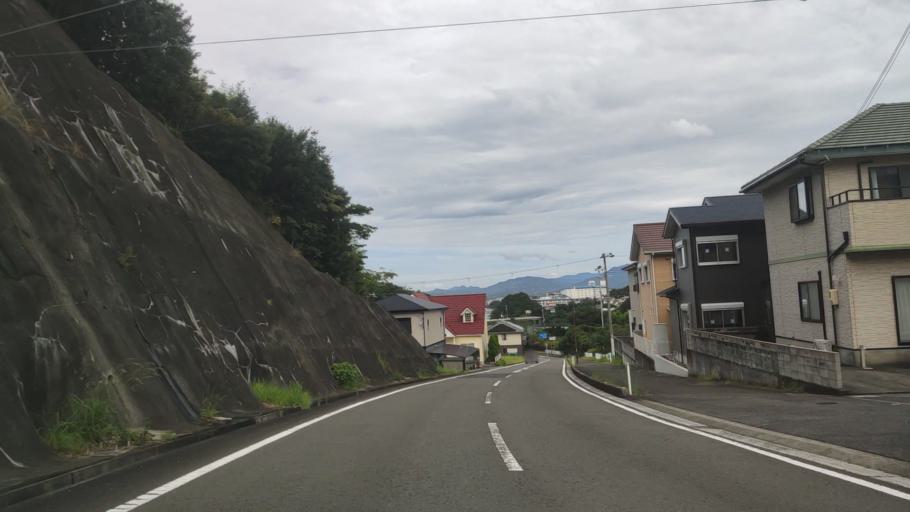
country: JP
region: Wakayama
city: Tanabe
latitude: 33.6886
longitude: 135.3882
